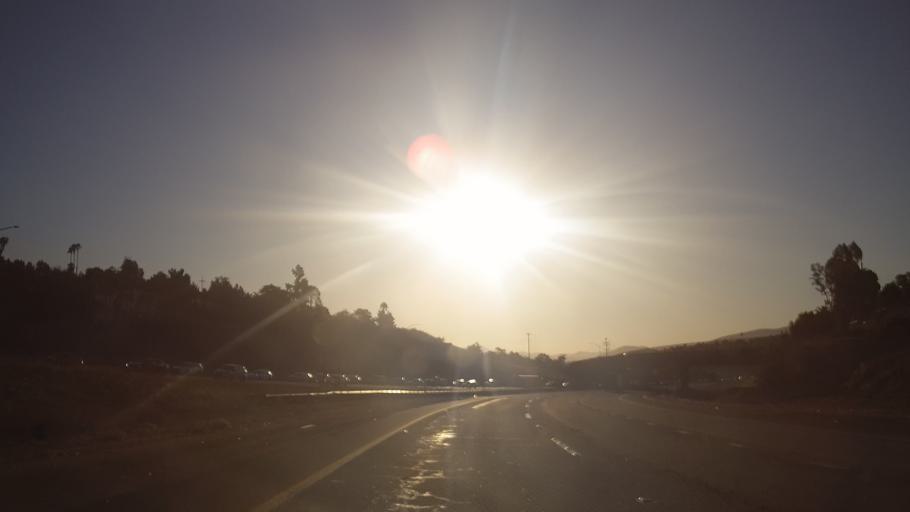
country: US
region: California
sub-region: San Diego County
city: Spring Valley
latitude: 32.7535
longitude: -117.0081
